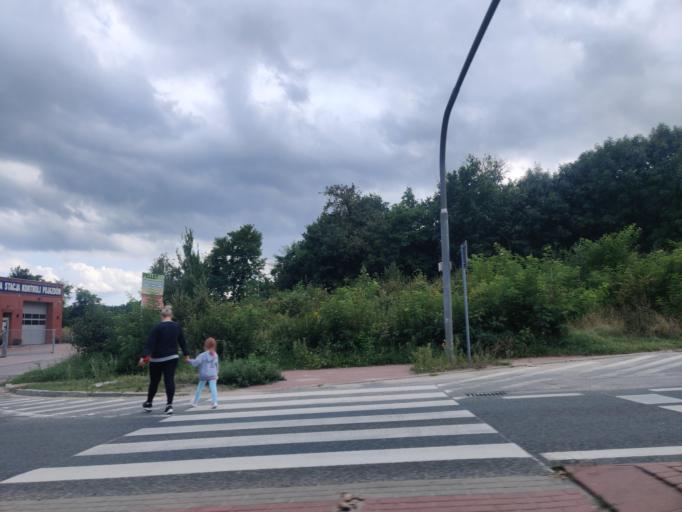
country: PL
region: Greater Poland Voivodeship
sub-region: Konin
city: Konin
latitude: 52.1977
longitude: 18.2985
